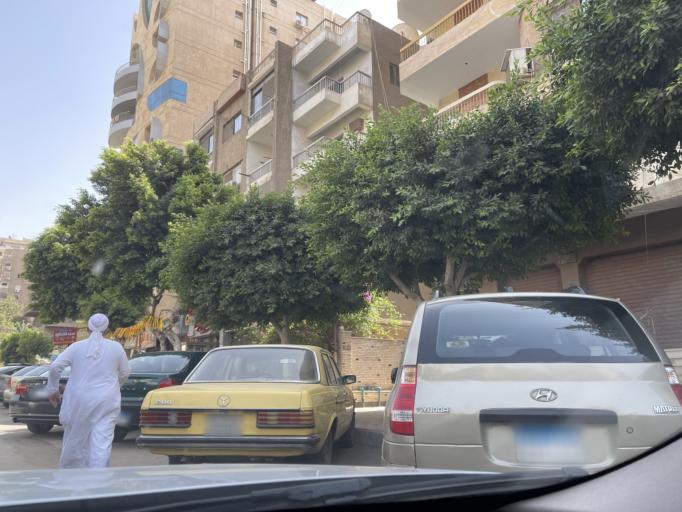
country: EG
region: Muhafazat al Qahirah
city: Cairo
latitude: 30.0664
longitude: 31.3500
